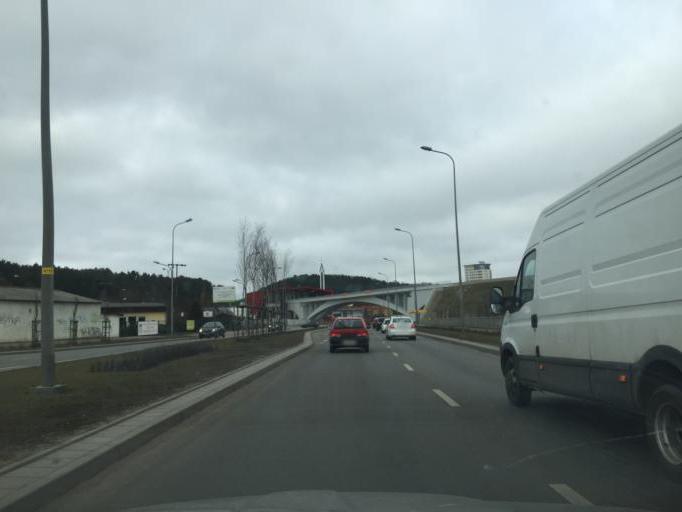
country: PL
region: Pomeranian Voivodeship
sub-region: Powiat gdanski
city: Kowale
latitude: 54.3754
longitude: 18.5694
